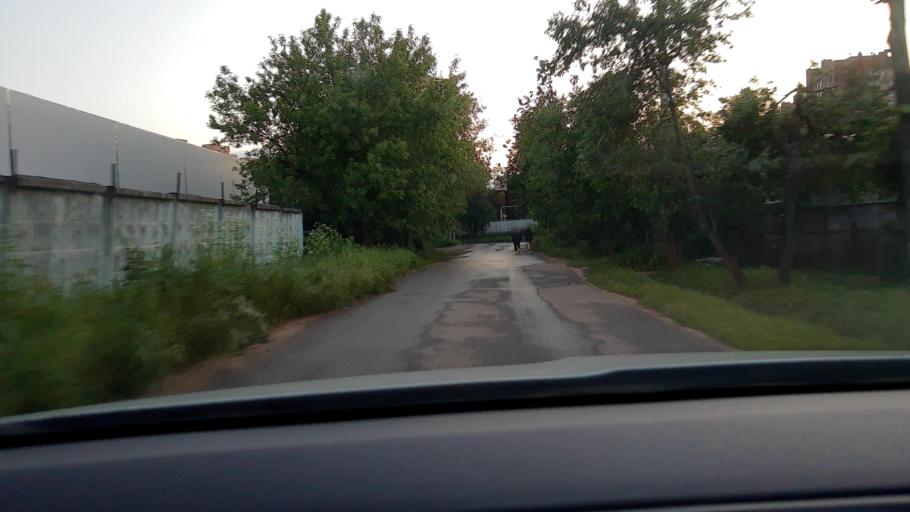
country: RU
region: Moskovskaya
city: Zvenigorod
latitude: 55.7390
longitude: 36.8605
